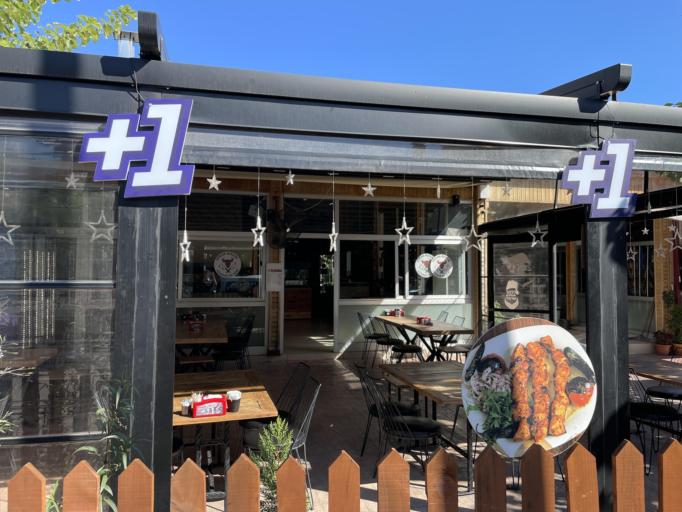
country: TR
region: Antalya
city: Kemer
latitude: 36.6039
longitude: 30.5587
